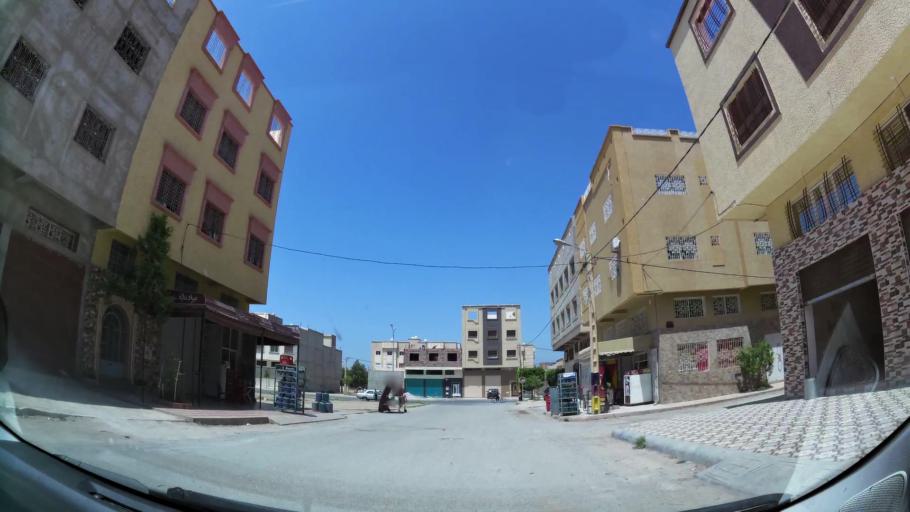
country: MA
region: Oriental
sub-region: Oujda-Angad
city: Oujda
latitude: 34.6958
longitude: -1.8854
